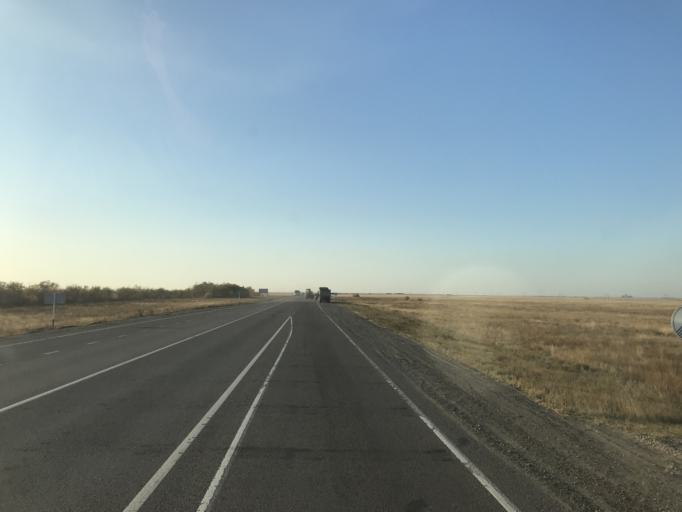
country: KZ
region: Pavlodar
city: Leninskiy
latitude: 52.1560
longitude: 76.8174
